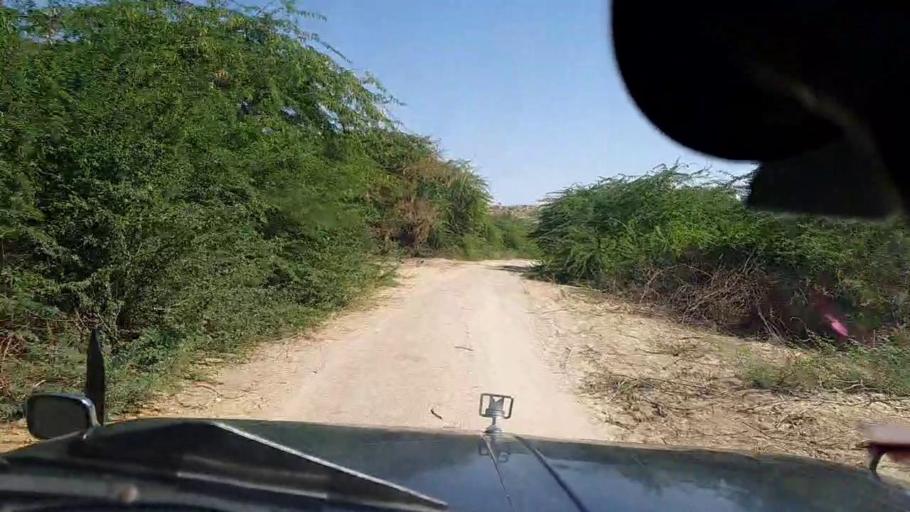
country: PK
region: Sindh
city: Diplo
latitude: 24.3920
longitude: 69.6558
